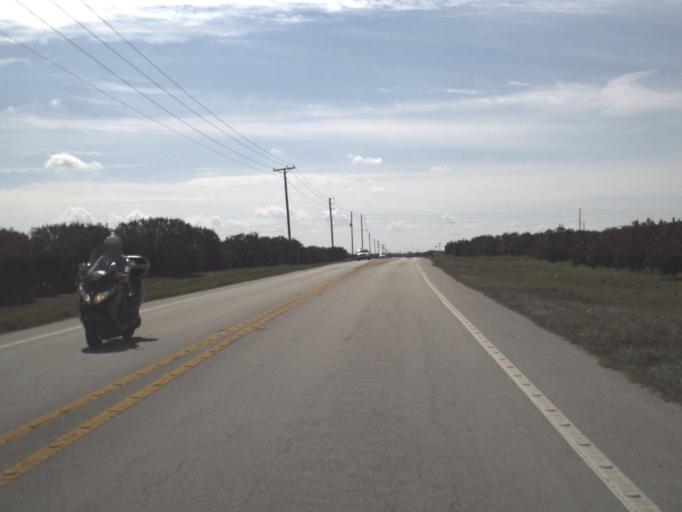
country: US
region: Florida
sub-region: Highlands County
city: Sebring
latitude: 27.5321
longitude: -81.4535
